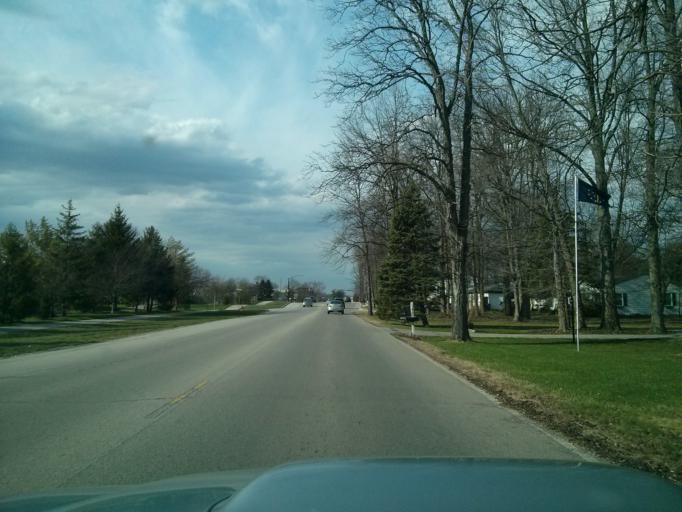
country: US
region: Indiana
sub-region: Hamilton County
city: Carmel
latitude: 39.9539
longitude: -86.1459
